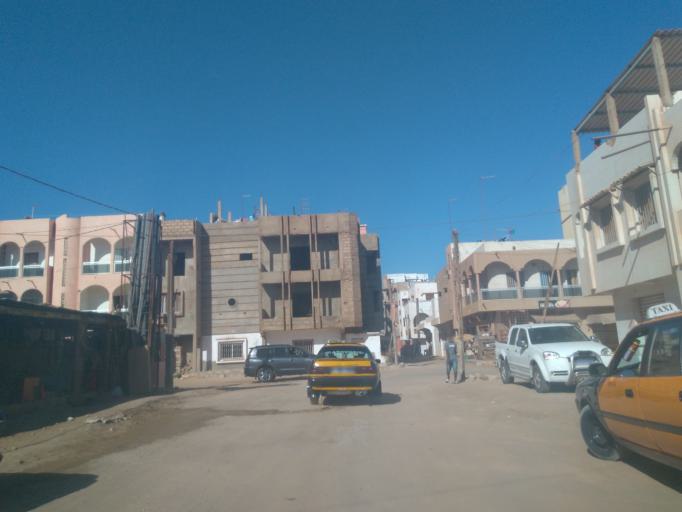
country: SN
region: Dakar
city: Pikine
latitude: 14.7736
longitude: -17.4184
